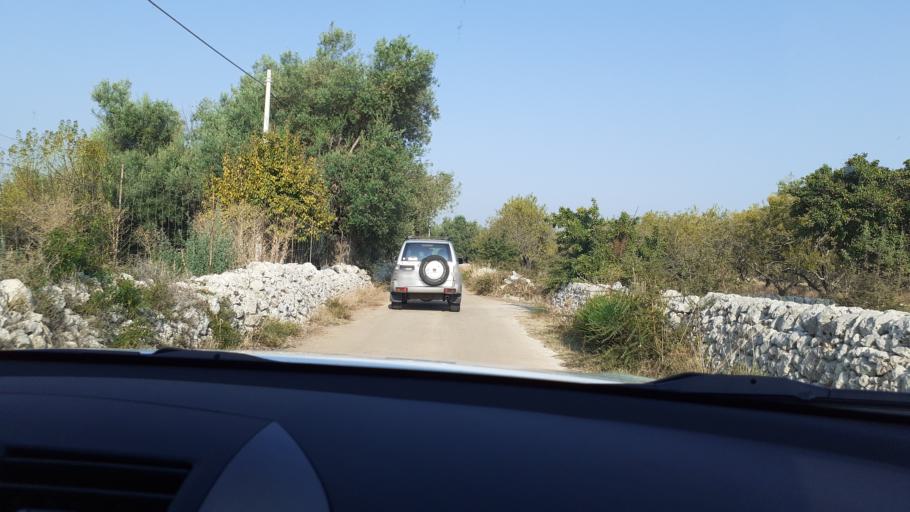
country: IT
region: Sicily
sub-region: Provincia di Siracusa
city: Cassibile
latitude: 36.9794
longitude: 15.1479
